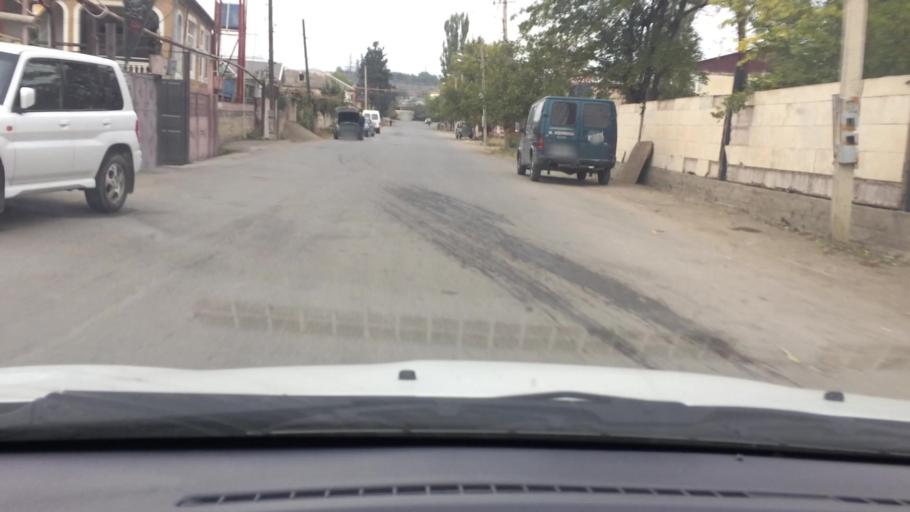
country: GE
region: Kvemo Kartli
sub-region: Marneuli
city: Marneuli
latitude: 41.4818
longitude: 44.7953
